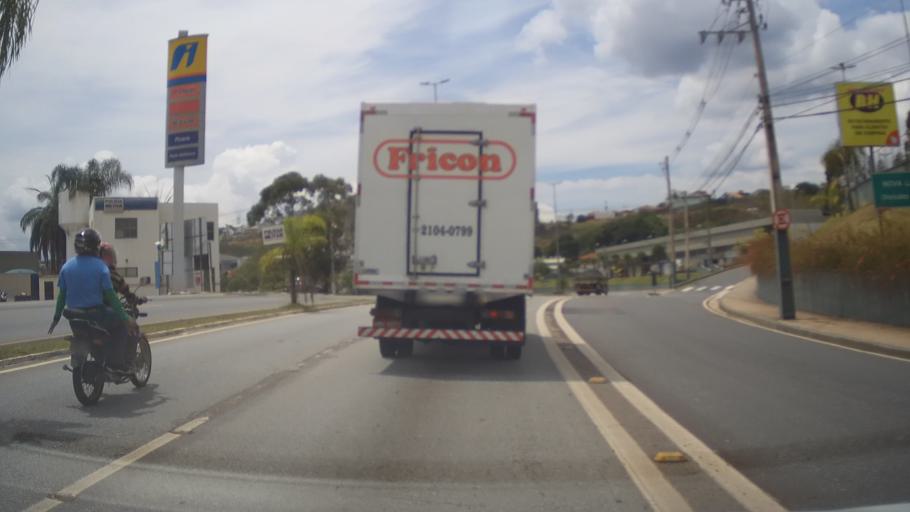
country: BR
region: Minas Gerais
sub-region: Nova Lima
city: Nova Lima
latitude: -19.9998
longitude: -43.8921
